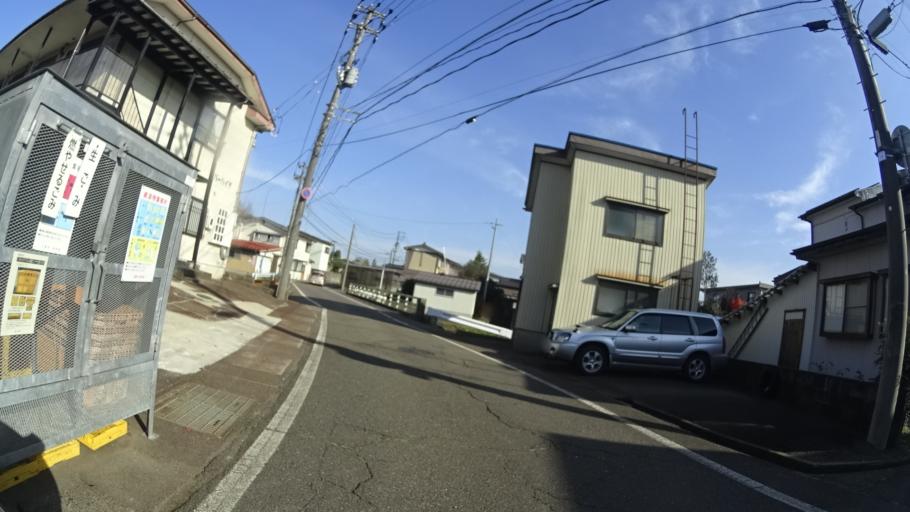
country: JP
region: Niigata
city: Joetsu
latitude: 37.1056
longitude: 138.2458
